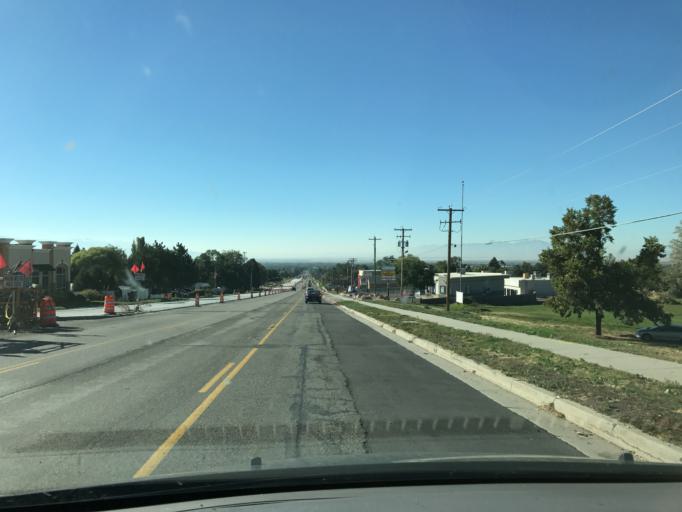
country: US
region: Utah
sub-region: Davis County
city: Hill Air Force Bace
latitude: 41.0995
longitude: -111.9735
